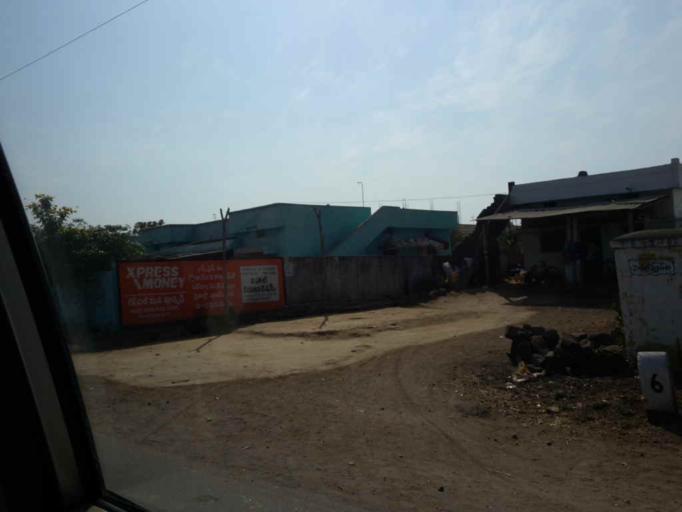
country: IN
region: Telangana
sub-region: Karimnagar
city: Jagtial
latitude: 18.8467
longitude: 78.8645
